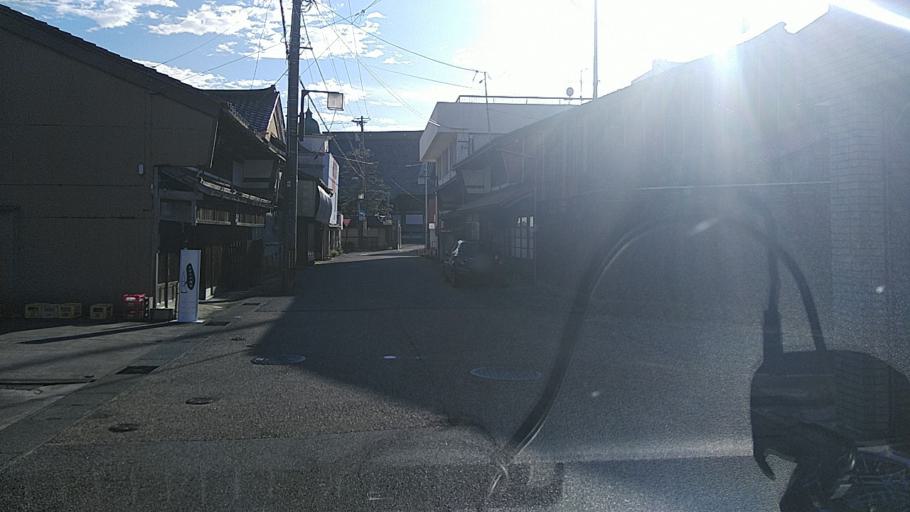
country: JP
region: Fukui
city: Maruoka
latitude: 36.3063
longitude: 136.3126
